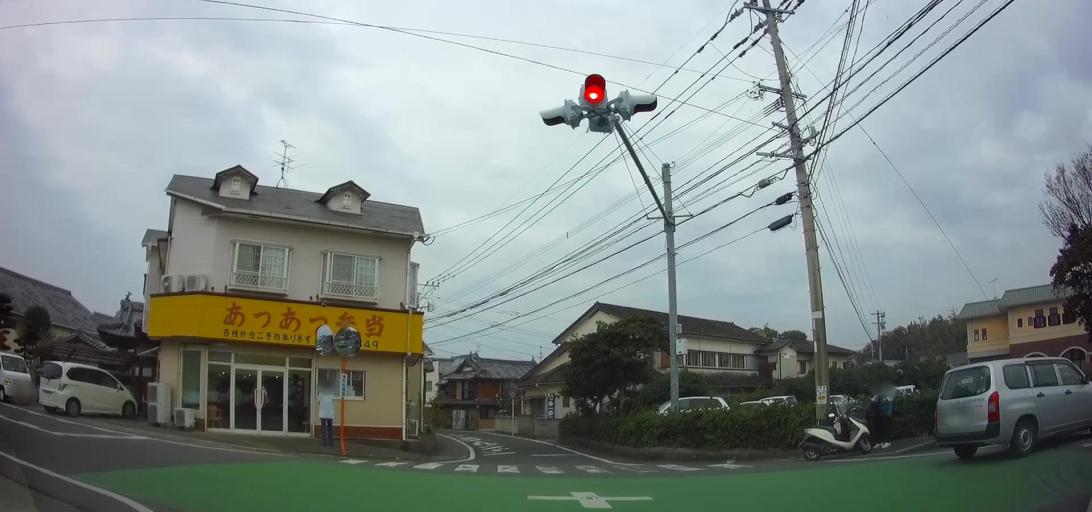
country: JP
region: Nagasaki
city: Shimabara
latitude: 32.6591
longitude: 130.2978
